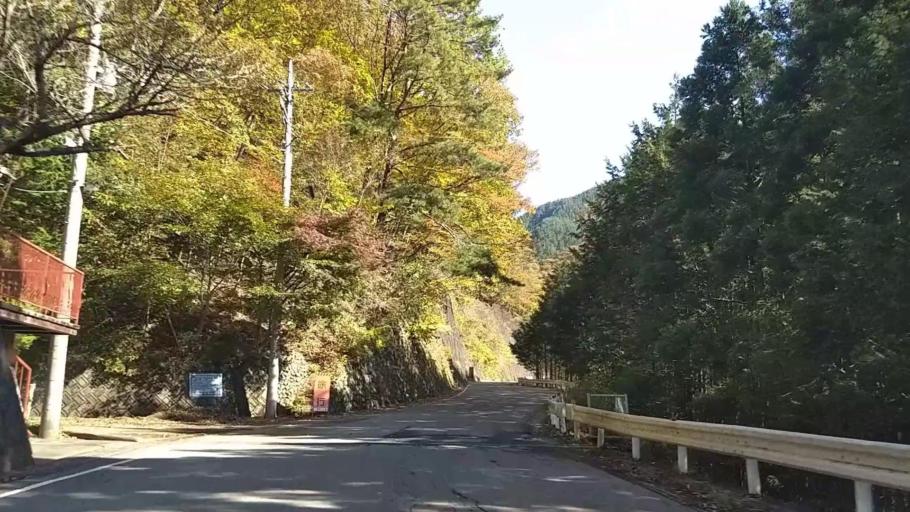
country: JP
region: Yamanashi
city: Otsuki
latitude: 35.7587
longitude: 138.9630
